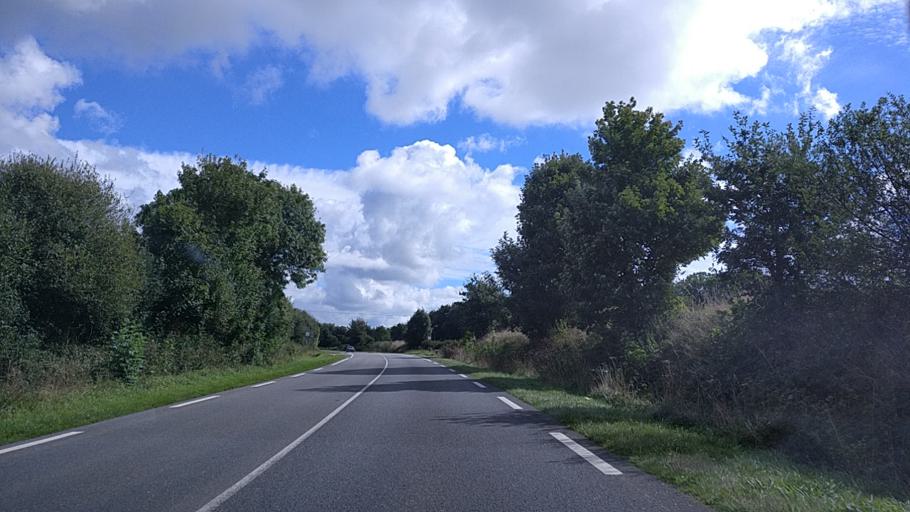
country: FR
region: Brittany
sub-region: Departement du Finistere
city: Gouesnou
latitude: 48.4419
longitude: -4.4529
